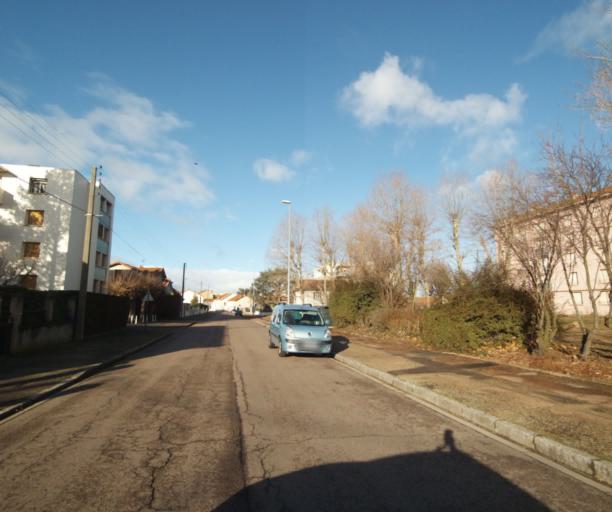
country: FR
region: Rhone-Alpes
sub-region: Departement de la Loire
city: Roanne
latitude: 46.0503
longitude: 4.0775
